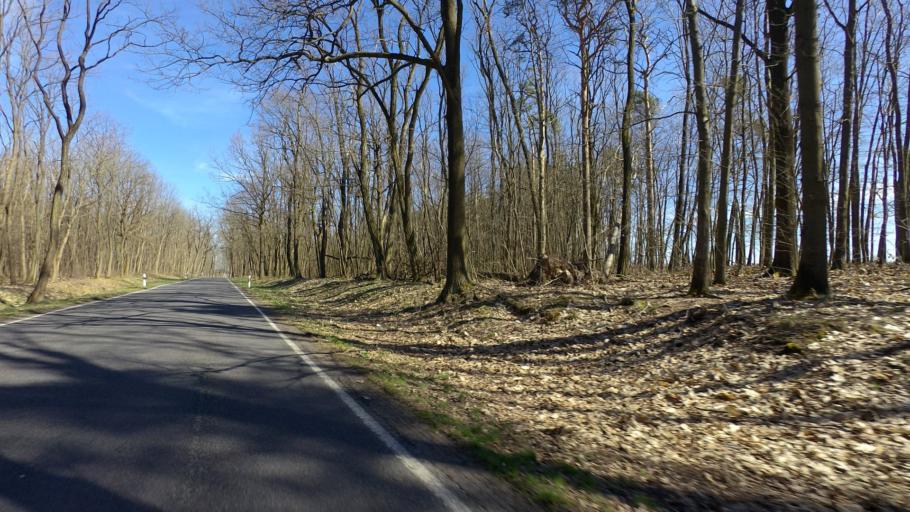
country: DE
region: Brandenburg
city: Munchehofe
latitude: 52.1564
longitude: 13.8615
